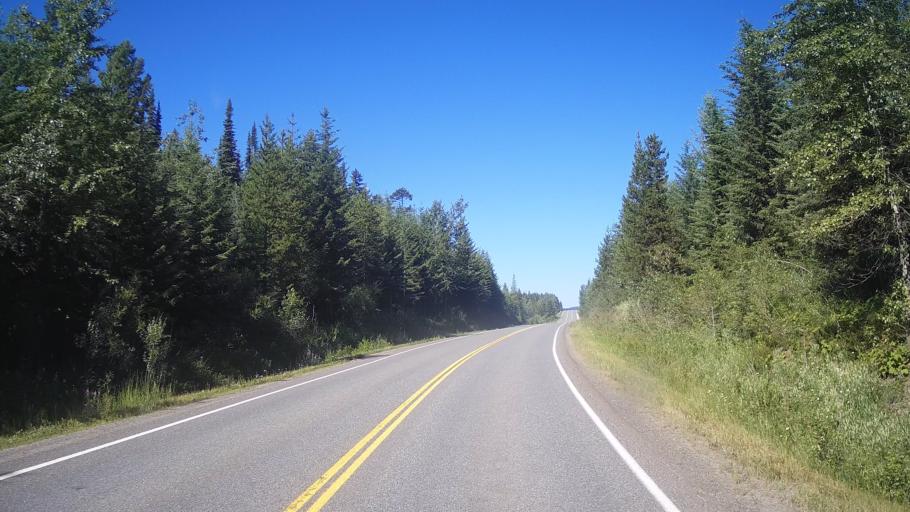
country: CA
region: British Columbia
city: Kamloops
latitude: 51.4981
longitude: -120.3636
